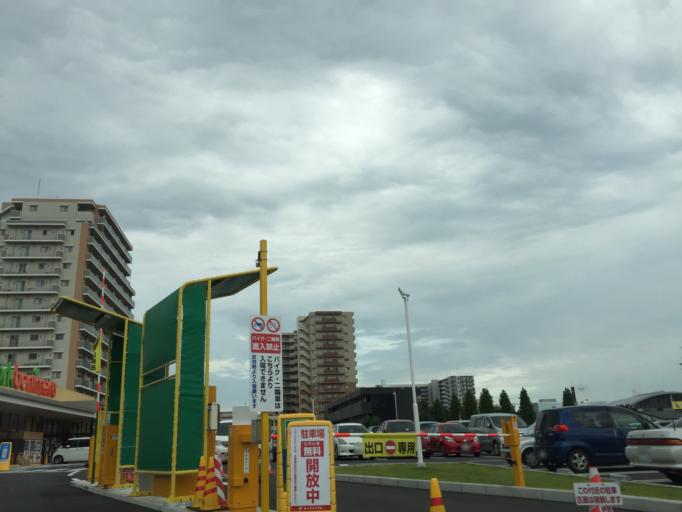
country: JP
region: Ibaraki
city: Naka
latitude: 36.0094
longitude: 140.1559
